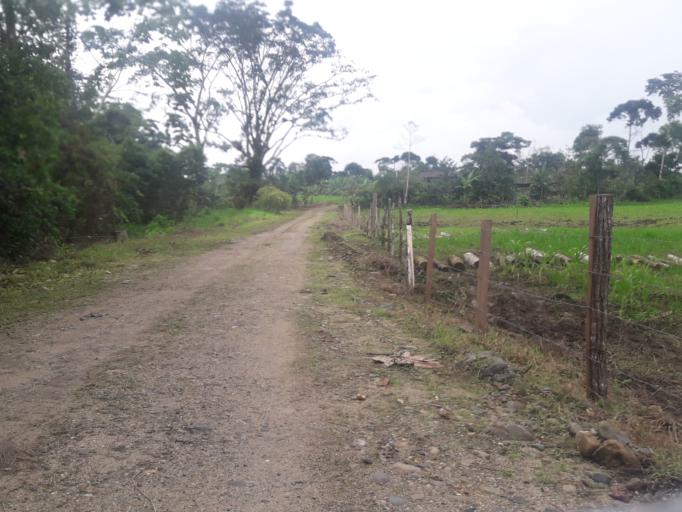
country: EC
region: Napo
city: Tena
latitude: -0.9788
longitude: -77.8448
